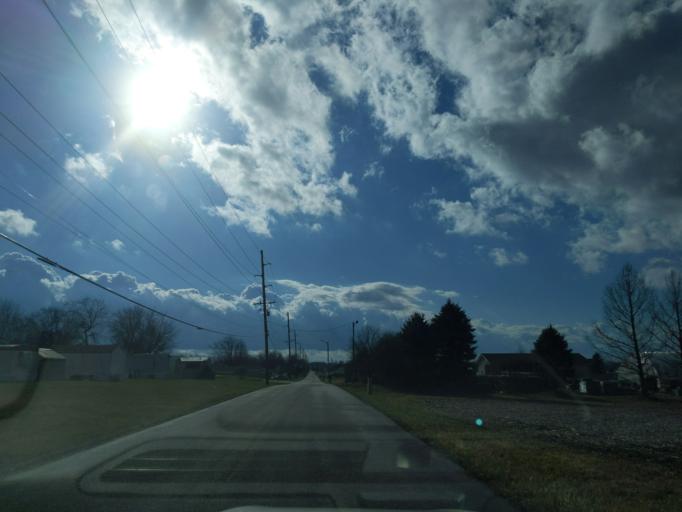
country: US
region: Indiana
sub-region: Decatur County
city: Greensburg
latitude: 39.3576
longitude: -85.4987
